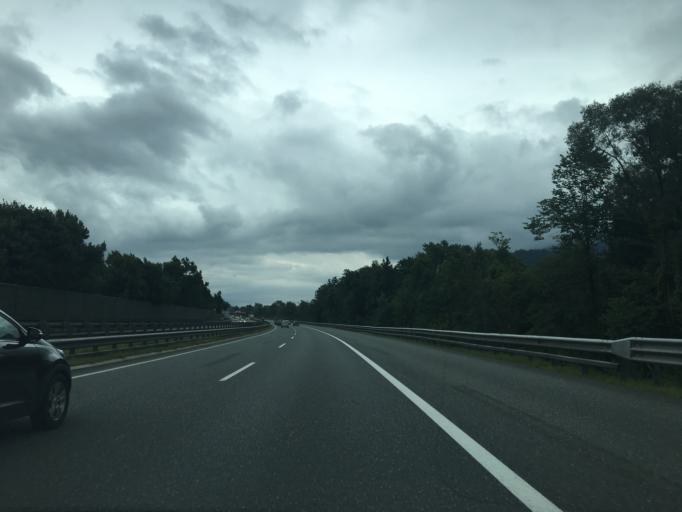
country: AT
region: Tyrol
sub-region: Politischer Bezirk Schwaz
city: Stans
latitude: 47.3657
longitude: 11.7283
